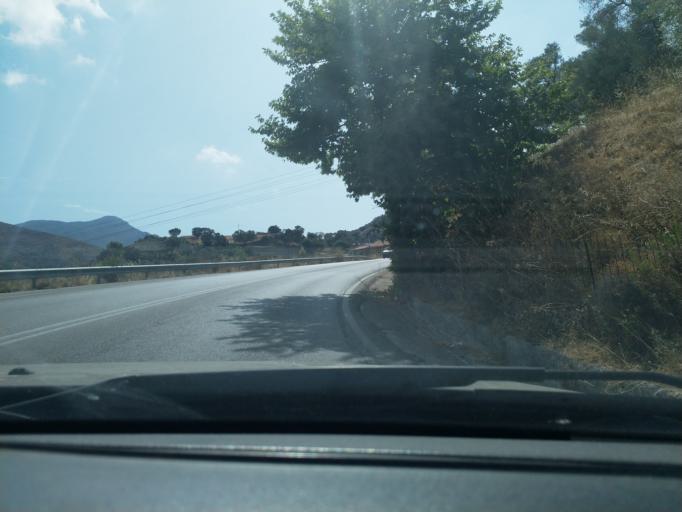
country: GR
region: Crete
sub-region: Nomos Rethymnis
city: Agia Foteini
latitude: 35.2195
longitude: 24.5086
